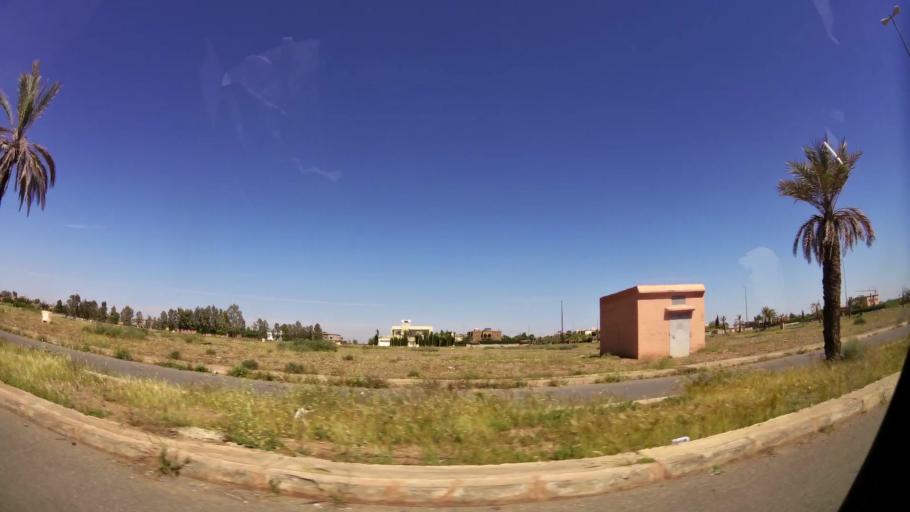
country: MA
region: Marrakech-Tensift-Al Haouz
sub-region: Marrakech
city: Marrakesh
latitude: 31.5866
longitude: -7.9999
